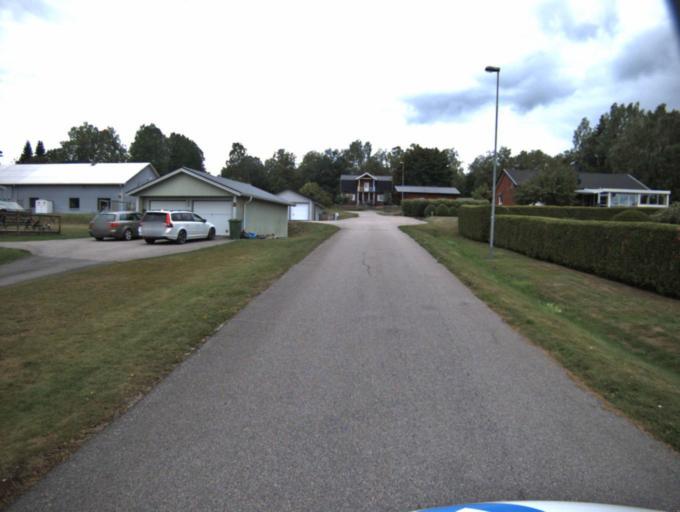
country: SE
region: Vaestra Goetaland
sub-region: Ulricehamns Kommun
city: Ulricehamn
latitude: 57.6700
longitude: 13.3679
